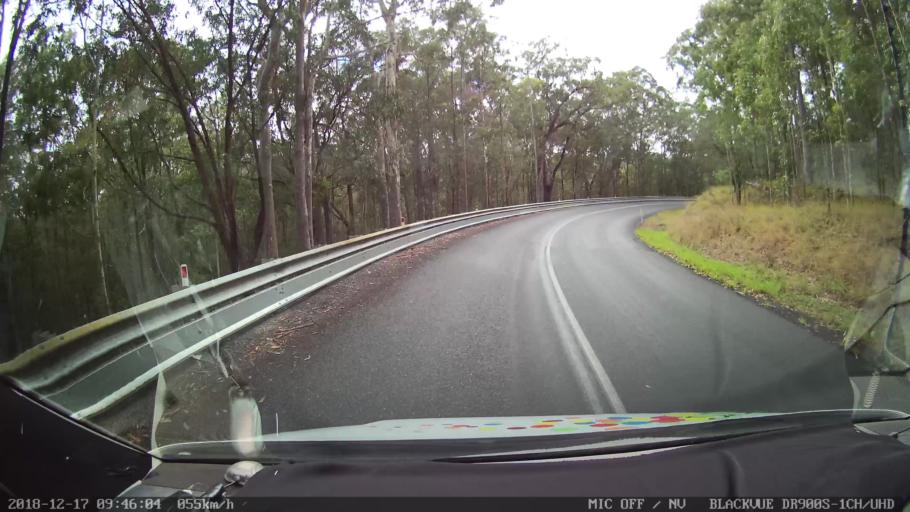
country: AU
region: New South Wales
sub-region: Tenterfield Municipality
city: Carrolls Creek
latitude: -28.9247
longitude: 152.3349
